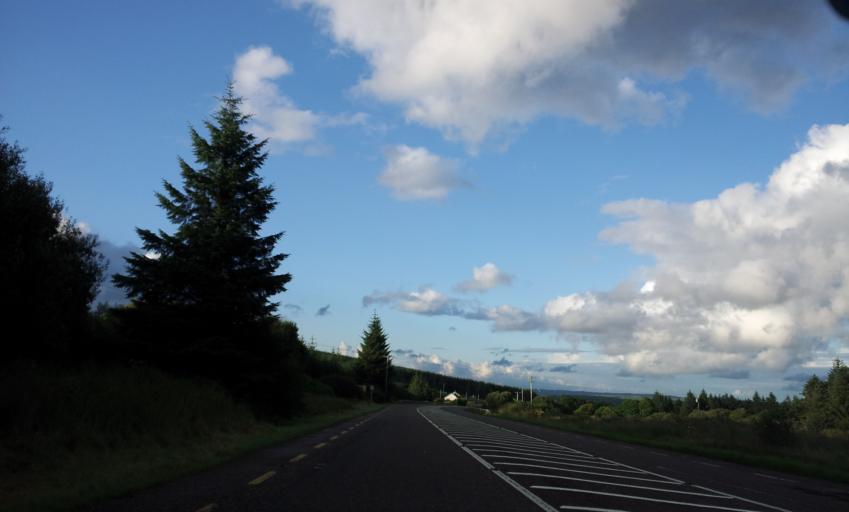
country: IE
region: Munster
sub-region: Ciarrai
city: Castleisland
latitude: 52.2724
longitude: -9.4168
